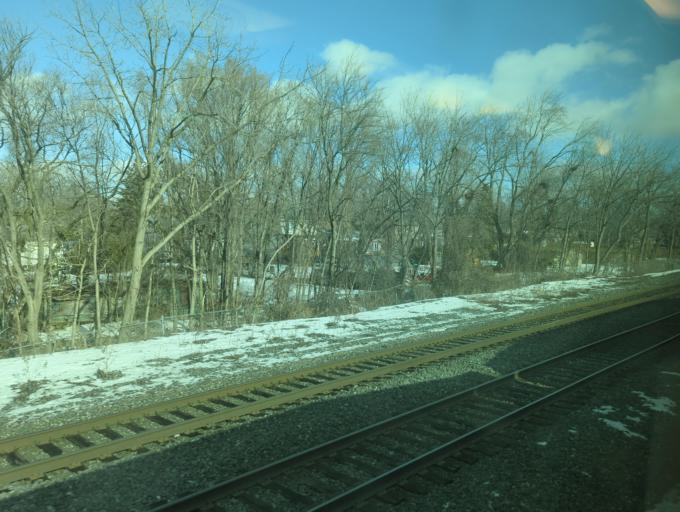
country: CA
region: Ontario
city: Burlington
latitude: 43.3422
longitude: -79.8074
